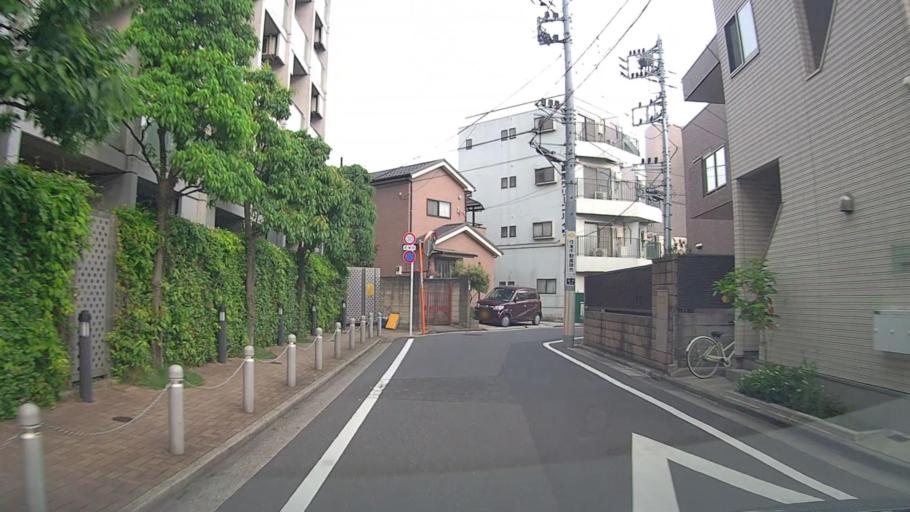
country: JP
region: Saitama
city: Kawaguchi
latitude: 35.7570
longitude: 139.7137
